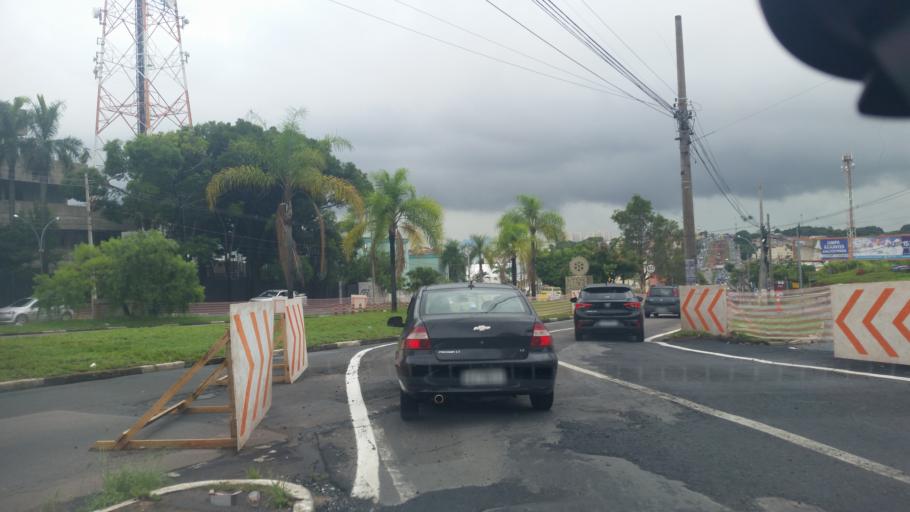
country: BR
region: Sao Paulo
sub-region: Campinas
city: Campinas
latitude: -22.9107
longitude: -47.0969
